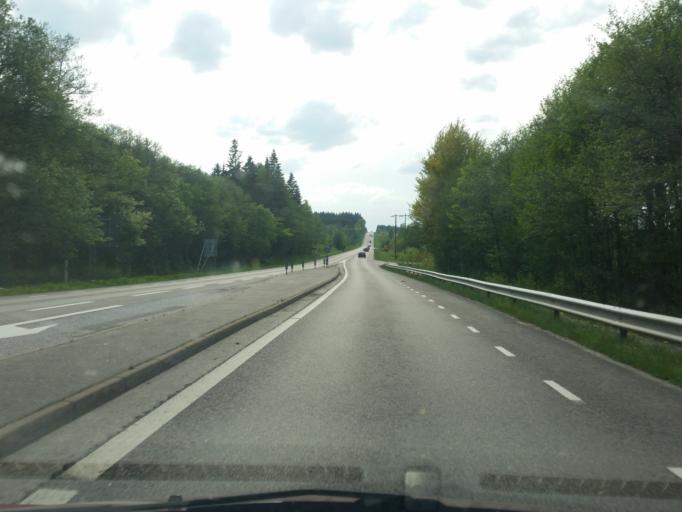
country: SE
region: Vaestra Goetaland
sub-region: Ulricehamns Kommun
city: Ulricehamn
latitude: 57.8075
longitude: 13.2390
